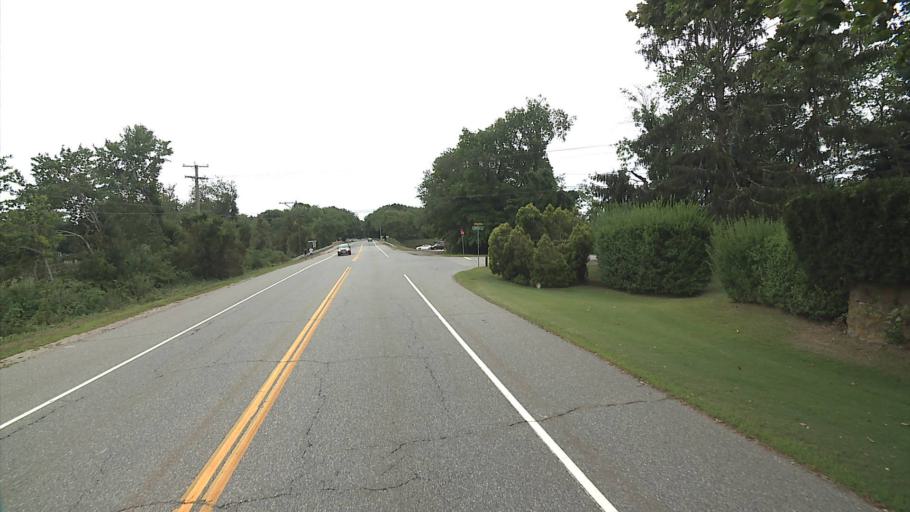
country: US
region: Connecticut
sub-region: Middlesex County
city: Old Saybrook Center
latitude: 41.3153
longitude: -72.3375
